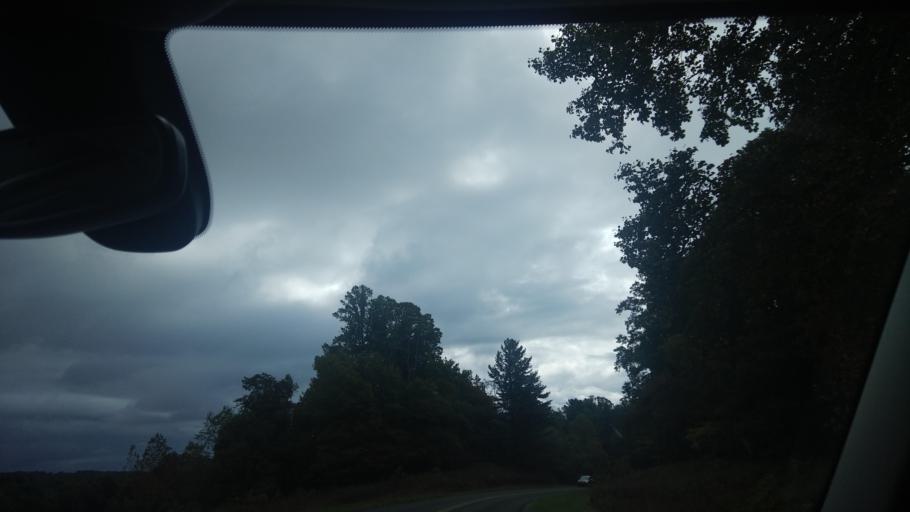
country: US
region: Virginia
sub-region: Carroll County
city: Cana
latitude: 36.6532
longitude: -80.5528
